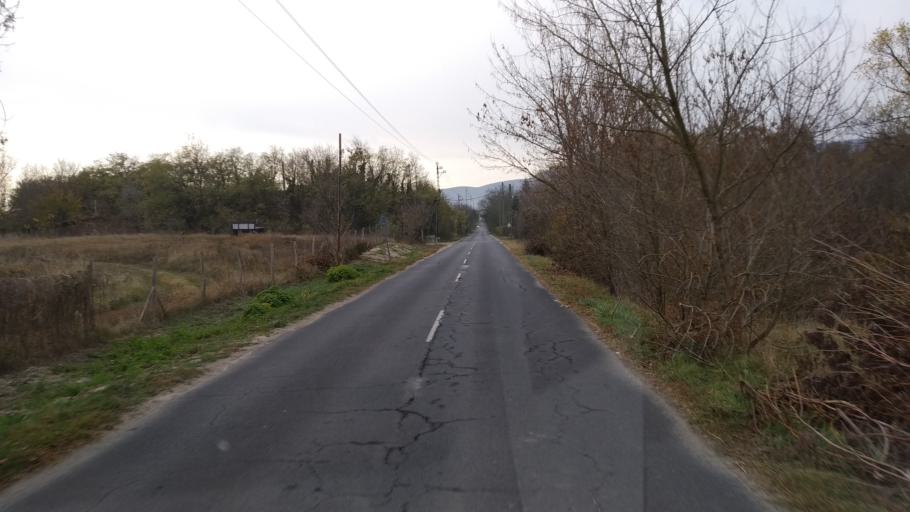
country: HU
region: Pest
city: Tahitotfalu
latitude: 47.7765
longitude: 19.0915
